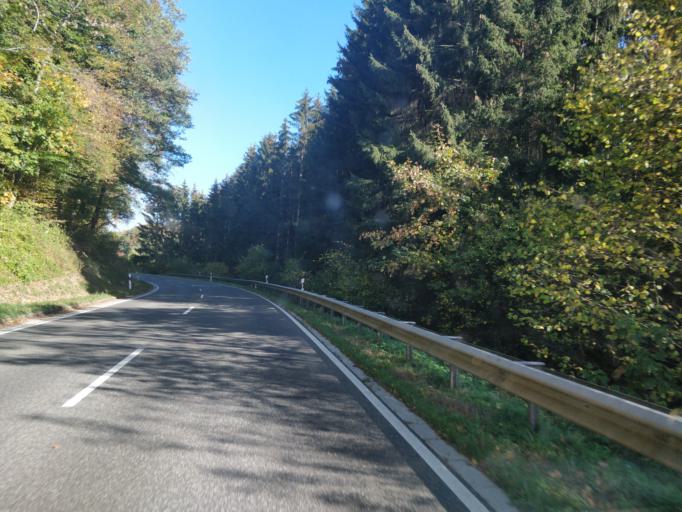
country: DE
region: North Rhine-Westphalia
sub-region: Regierungsbezirk Koln
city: Nettersheim
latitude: 50.5234
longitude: 6.6805
